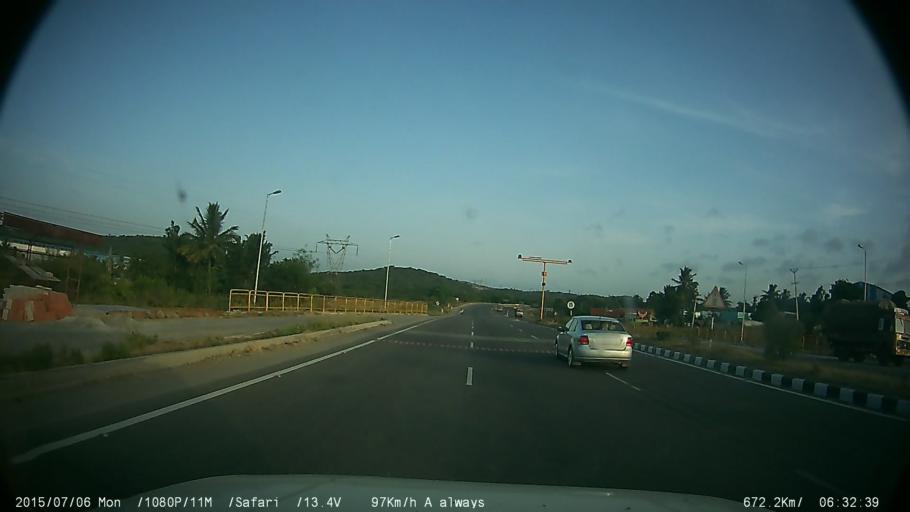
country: IN
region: Tamil Nadu
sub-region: Krishnagiri
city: Hosur
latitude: 12.6877
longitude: 77.9254
